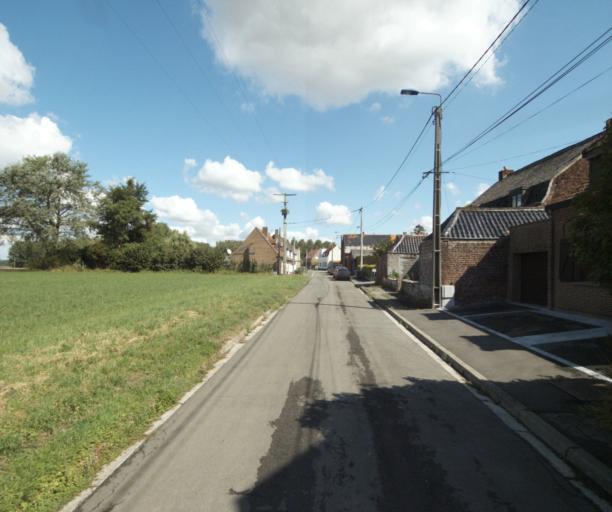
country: FR
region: Nord-Pas-de-Calais
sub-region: Departement du Nord
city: Willems
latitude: 50.6358
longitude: 3.2401
